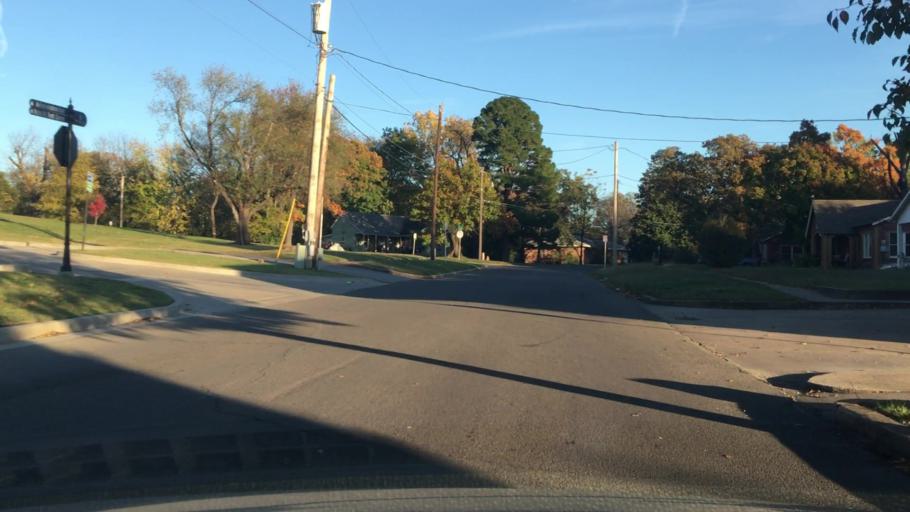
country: US
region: Oklahoma
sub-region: Cherokee County
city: Tahlequah
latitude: 35.9183
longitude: -94.9684
